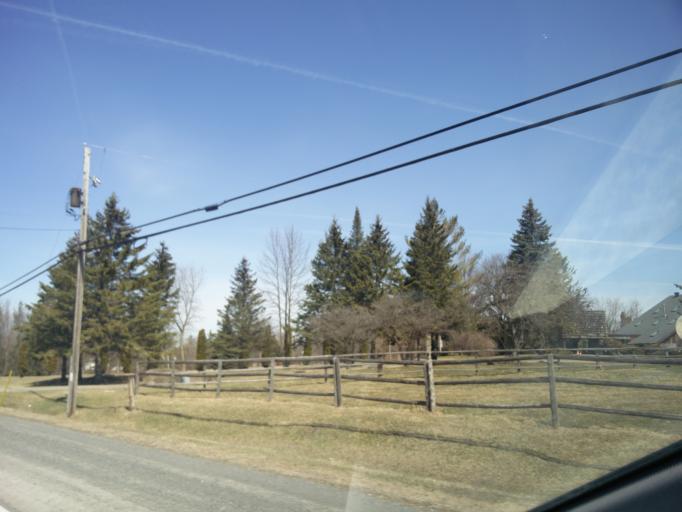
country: CA
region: Ontario
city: Bells Corners
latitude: 45.2051
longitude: -75.6529
